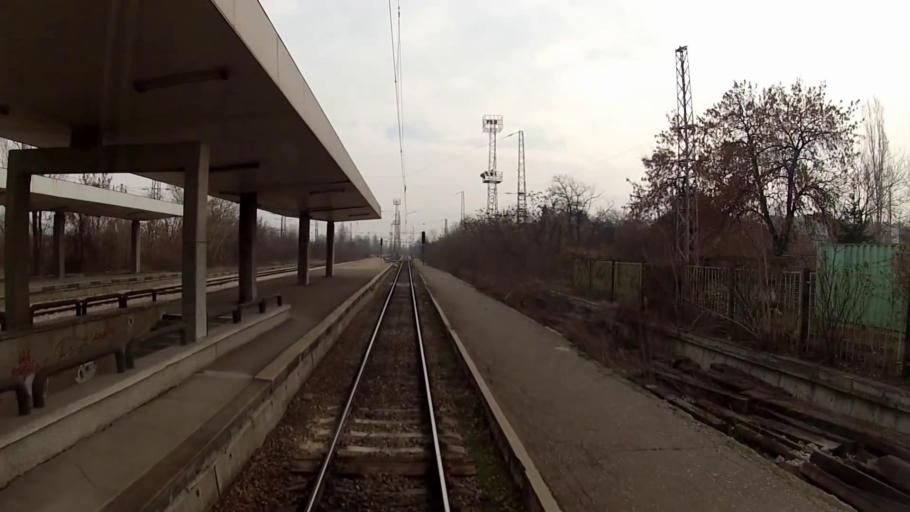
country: BG
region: Sofia-Capital
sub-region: Stolichna Obshtina
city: Sofia
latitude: 42.6888
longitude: 23.3765
